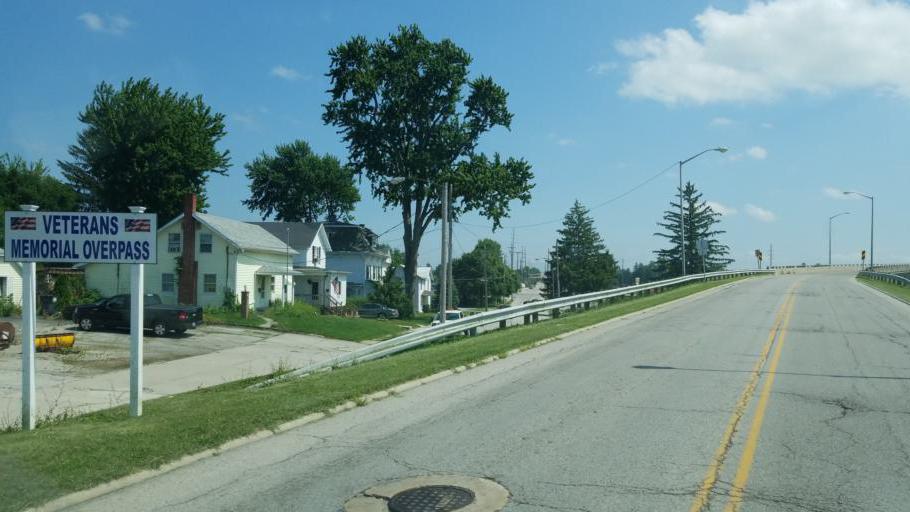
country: US
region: Ohio
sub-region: Huron County
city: Bellevue
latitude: 41.2720
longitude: -82.8392
